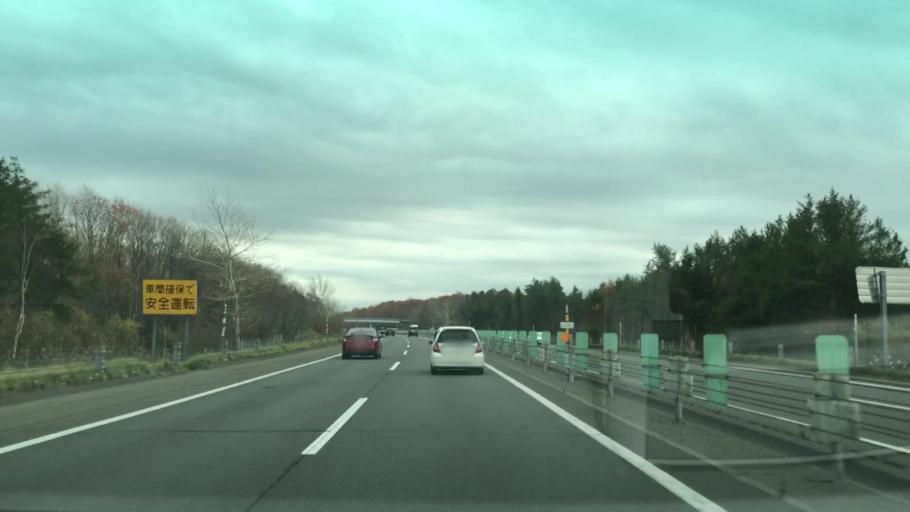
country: JP
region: Hokkaido
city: Chitose
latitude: 42.8537
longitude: 141.5659
